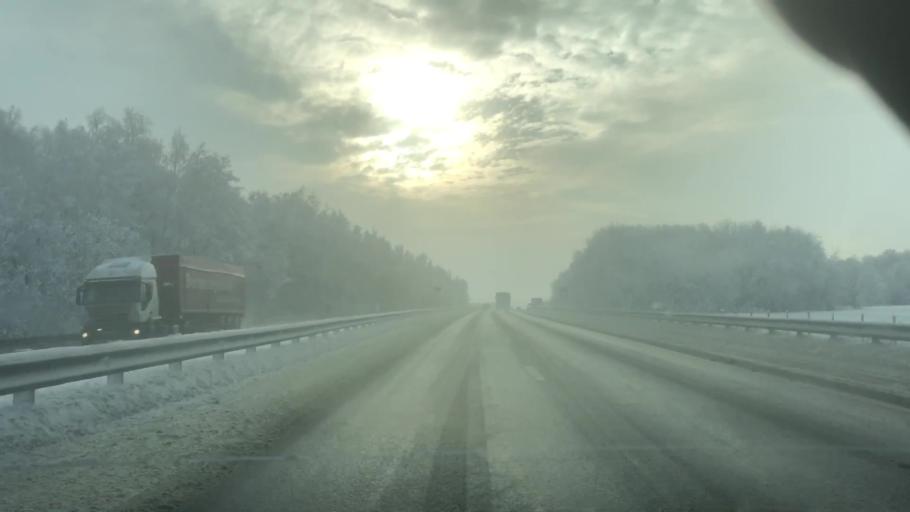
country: RU
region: Tula
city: Venev
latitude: 54.3824
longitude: 38.1550
